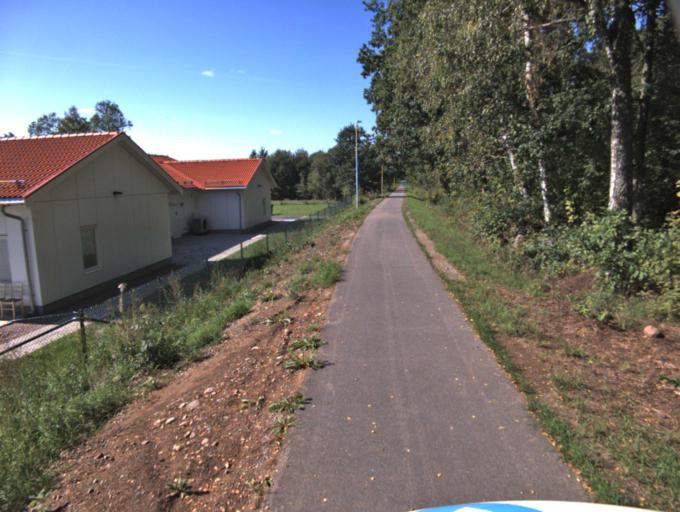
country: SE
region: Vaestra Goetaland
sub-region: Ulricehamns Kommun
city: Ulricehamn
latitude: 57.7989
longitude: 13.3902
